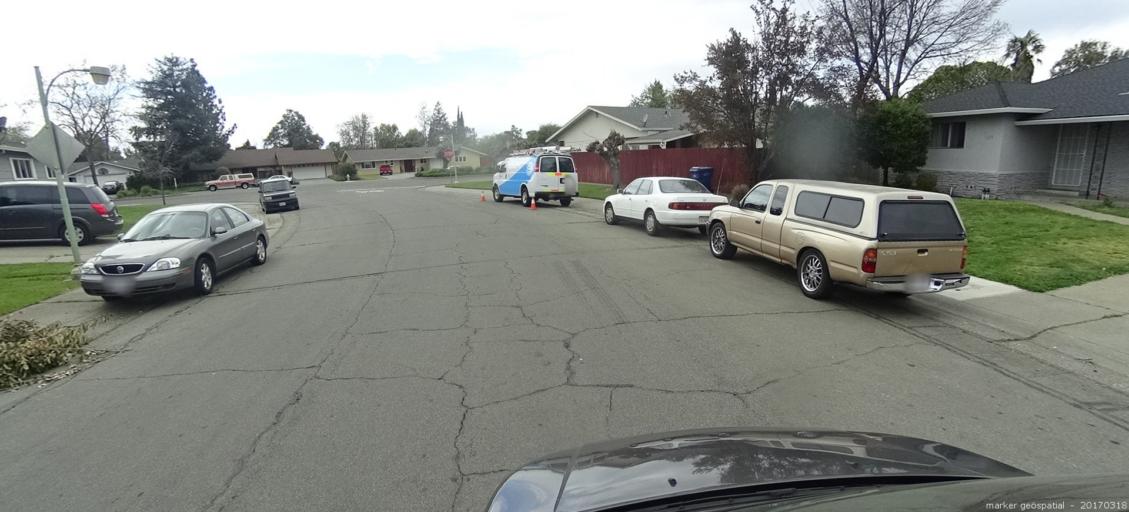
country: US
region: California
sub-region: Sacramento County
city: Parkway
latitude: 38.4800
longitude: -121.4395
